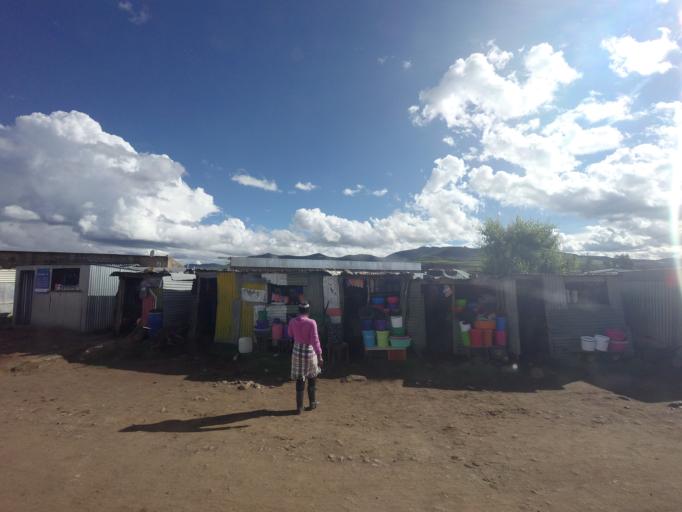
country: LS
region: Maseru
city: Nako
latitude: -29.8404
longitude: 28.0514
